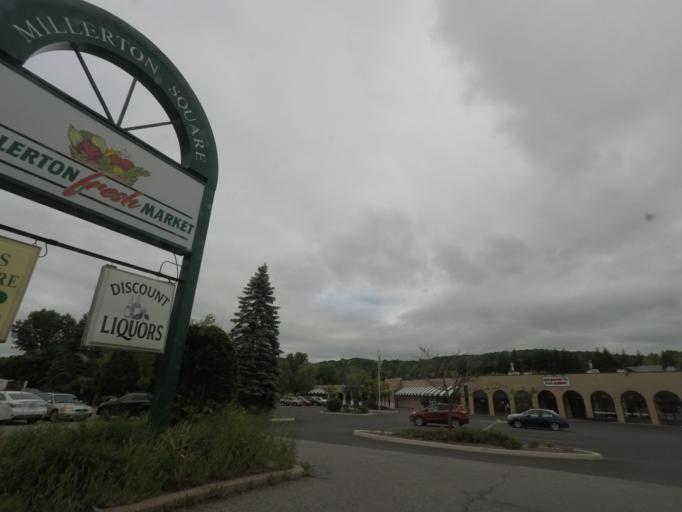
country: US
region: New York
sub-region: Dutchess County
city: Pine Plains
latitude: 41.9525
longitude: -73.5029
